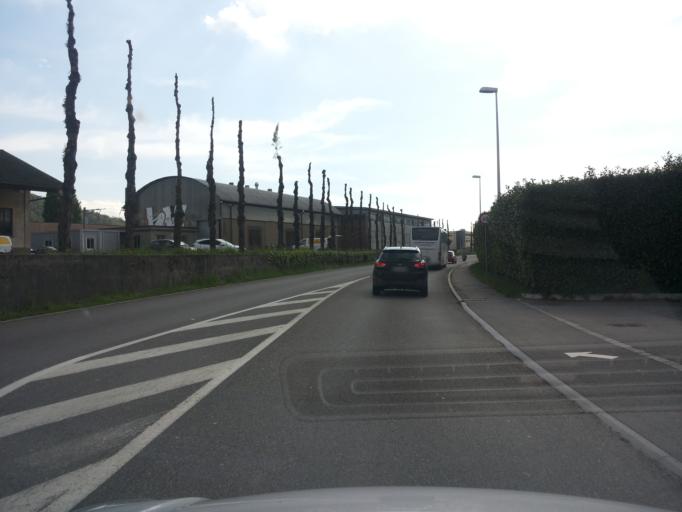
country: CH
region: Ticino
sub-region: Mendrisio District
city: Stabio
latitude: 45.8499
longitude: 8.9432
